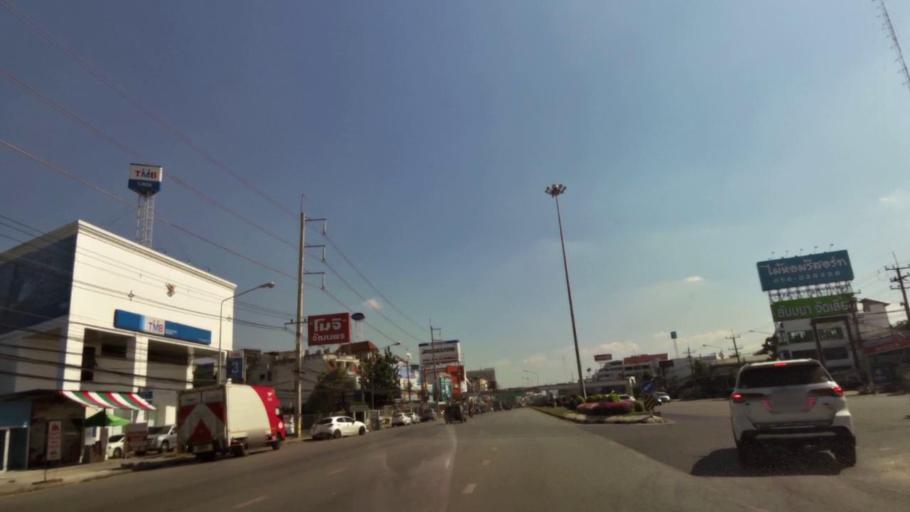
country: TH
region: Nakhon Sawan
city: Nakhon Sawan
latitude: 15.7019
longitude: 100.1167
